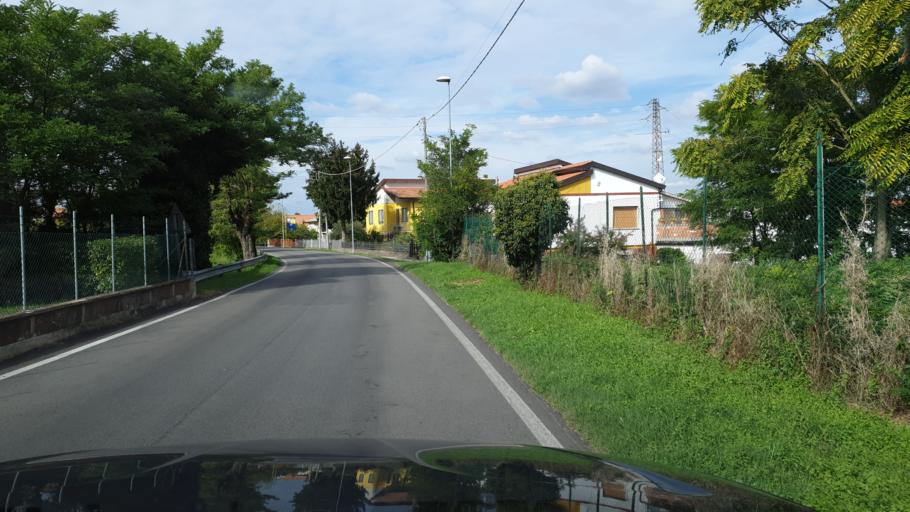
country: IT
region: Veneto
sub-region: Provincia di Rovigo
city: Costa di Rovigo
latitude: 45.0512
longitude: 11.6977
